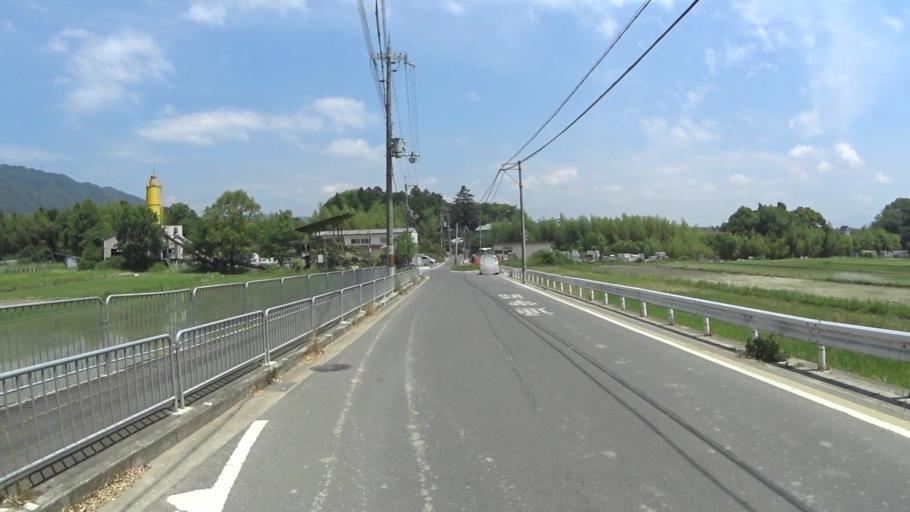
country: JP
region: Kyoto
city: Muko
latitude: 34.9487
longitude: 135.6662
